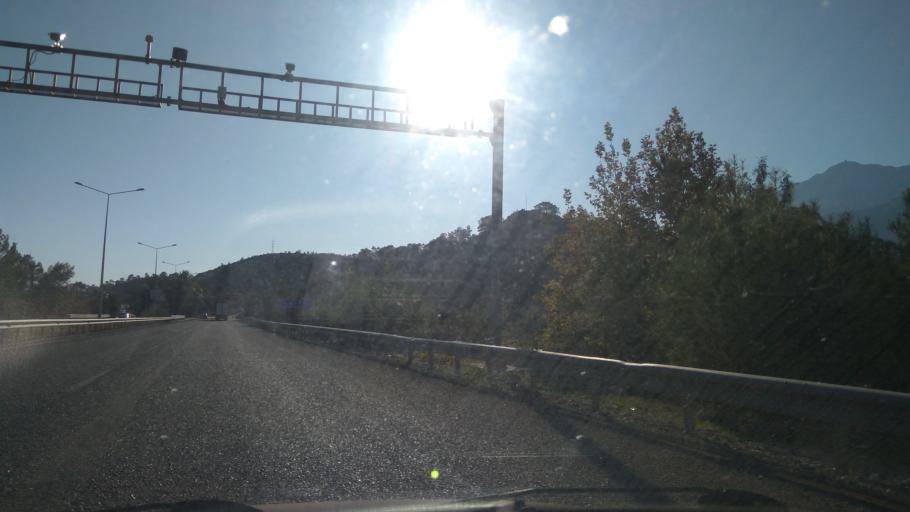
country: TR
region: Antalya
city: Kemer
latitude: 36.5739
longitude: 30.5545
